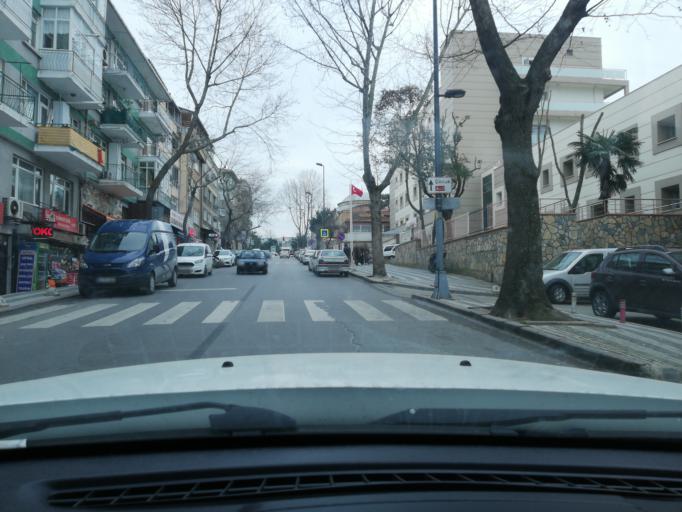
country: TR
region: Istanbul
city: UEskuedar
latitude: 41.0158
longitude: 29.0267
